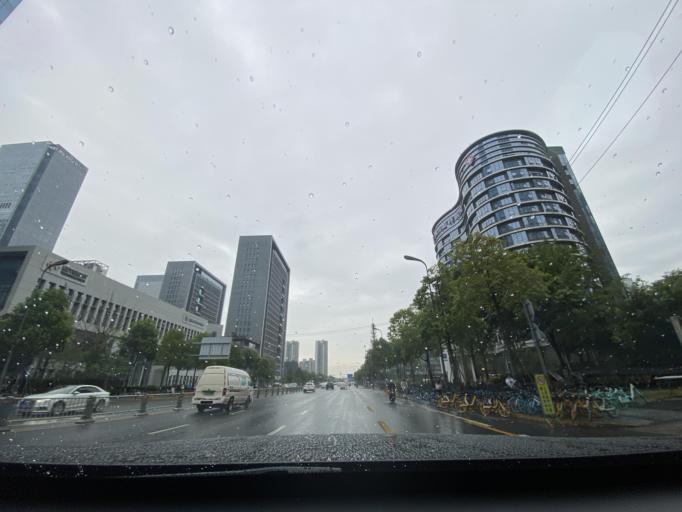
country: CN
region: Sichuan
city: Chengdu
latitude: 30.5447
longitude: 104.0619
